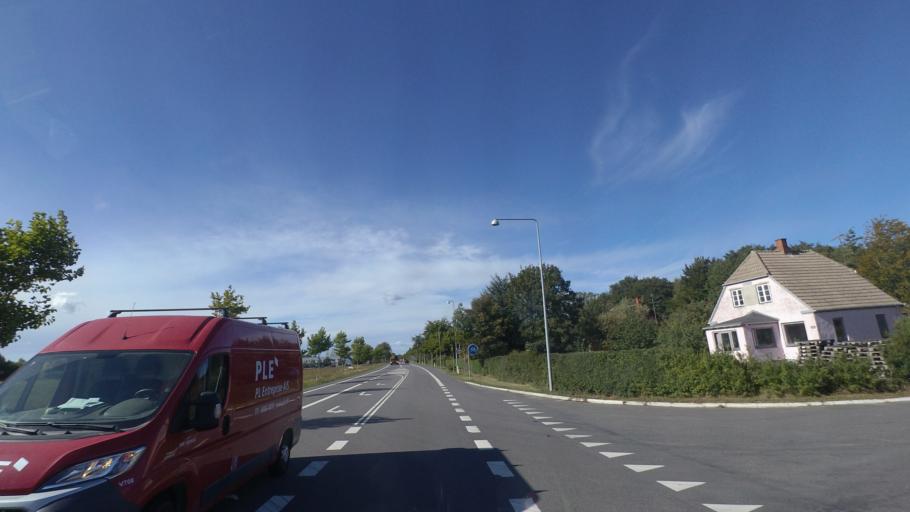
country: DK
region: Capital Region
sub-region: Bornholm Kommune
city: Ronne
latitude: 55.0910
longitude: 14.7352
